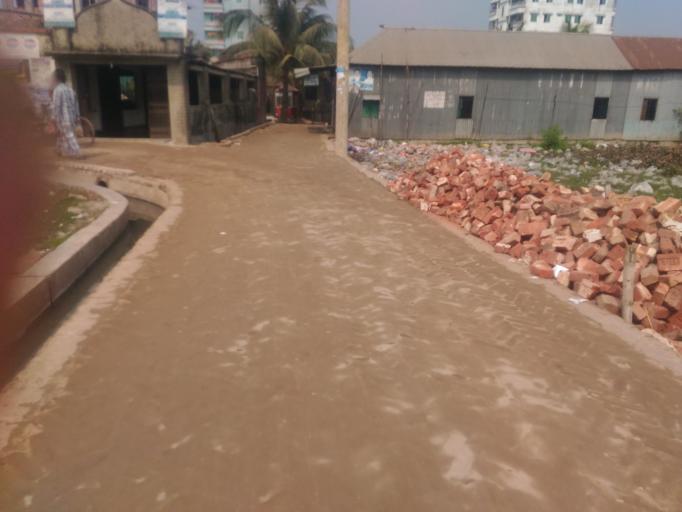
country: BD
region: Dhaka
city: Tungi
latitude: 23.9917
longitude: 90.3775
